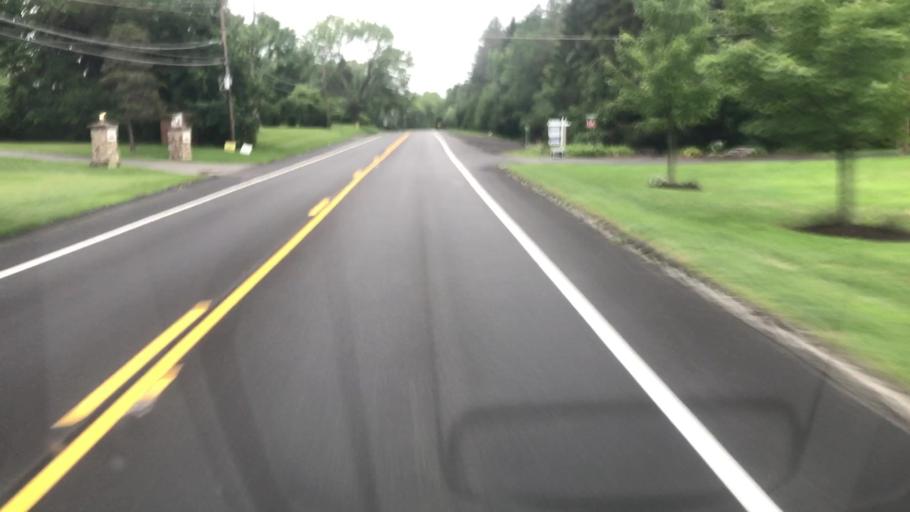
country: US
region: New York
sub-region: Cayuga County
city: Melrose Park
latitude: 42.8992
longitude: -76.5250
